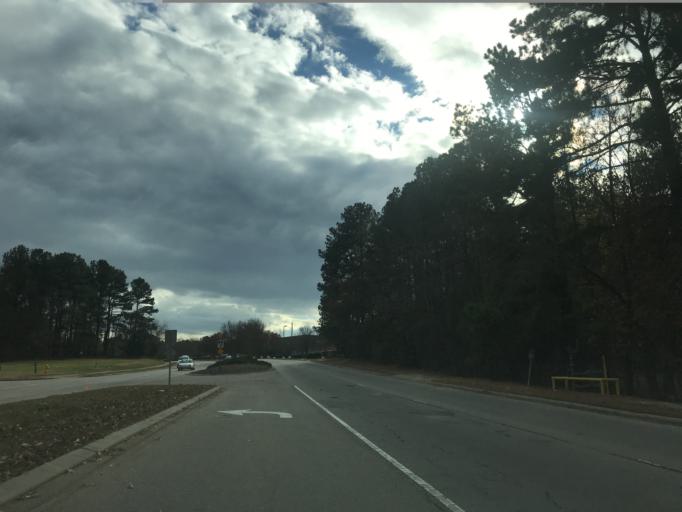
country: US
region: North Carolina
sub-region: Wake County
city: Raleigh
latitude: 35.7741
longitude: -78.5604
